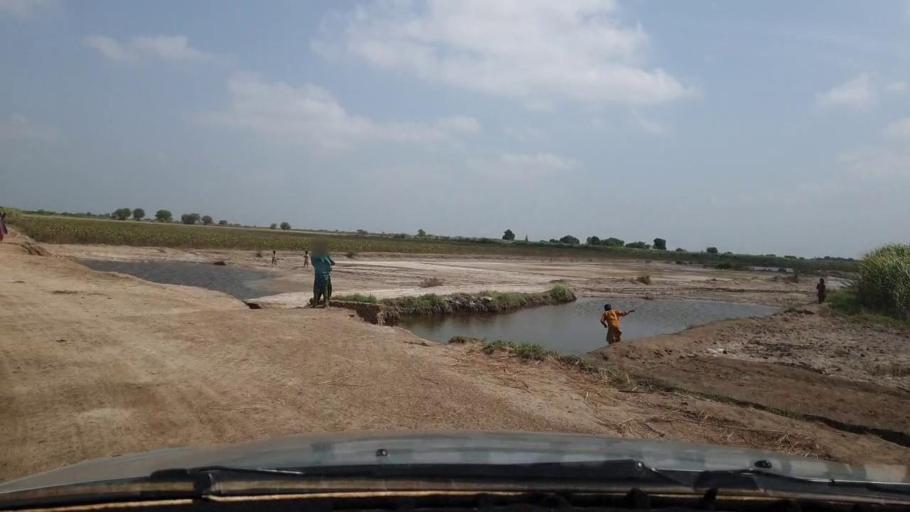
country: PK
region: Sindh
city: Matli
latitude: 25.1030
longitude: 68.6417
